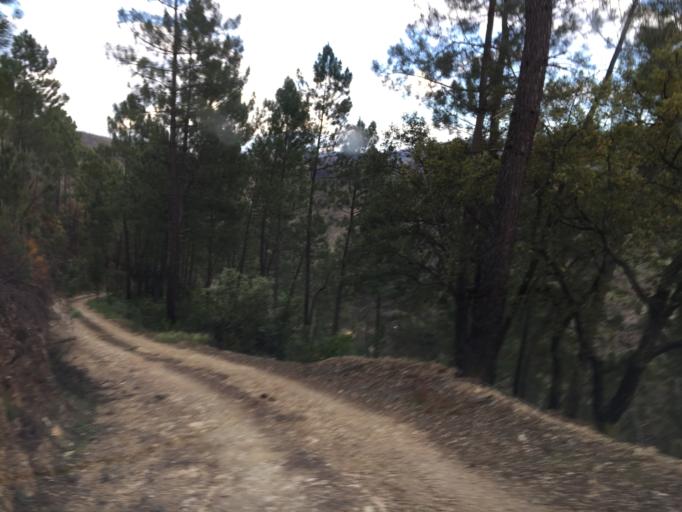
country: PT
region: Coimbra
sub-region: Pampilhosa da Serra
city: Pampilhosa da Serra
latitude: 40.0480
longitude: -7.9441
